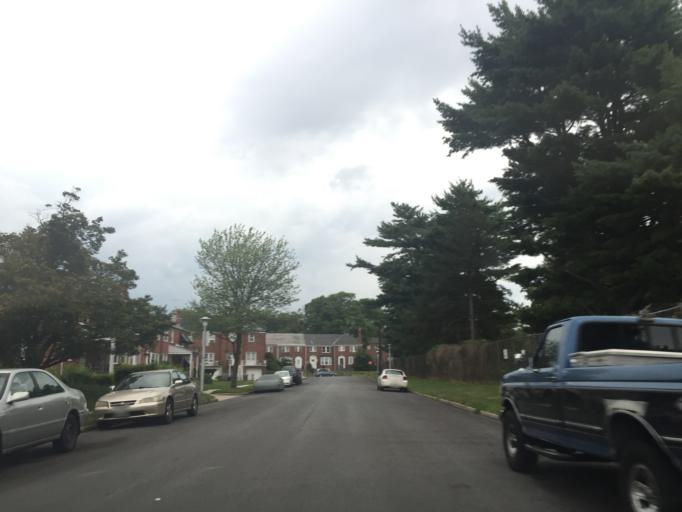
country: US
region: Maryland
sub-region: City of Baltimore
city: Baltimore
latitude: 39.3367
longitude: -76.5921
